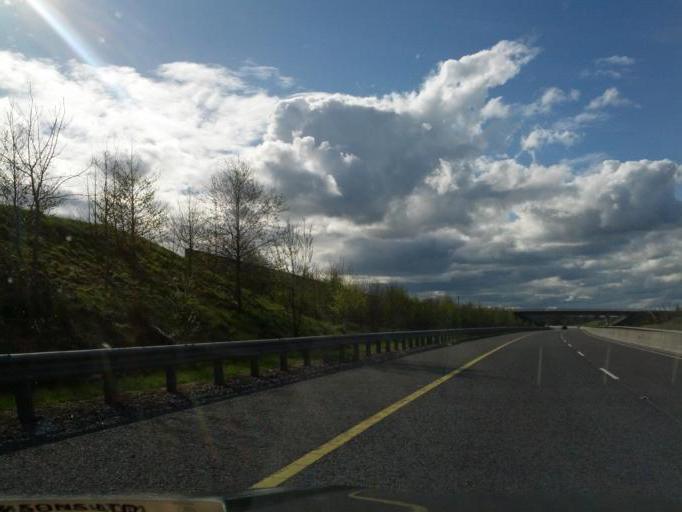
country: IE
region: Leinster
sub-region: Uibh Fhaili
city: Clara
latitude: 53.3880
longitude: -7.6046
